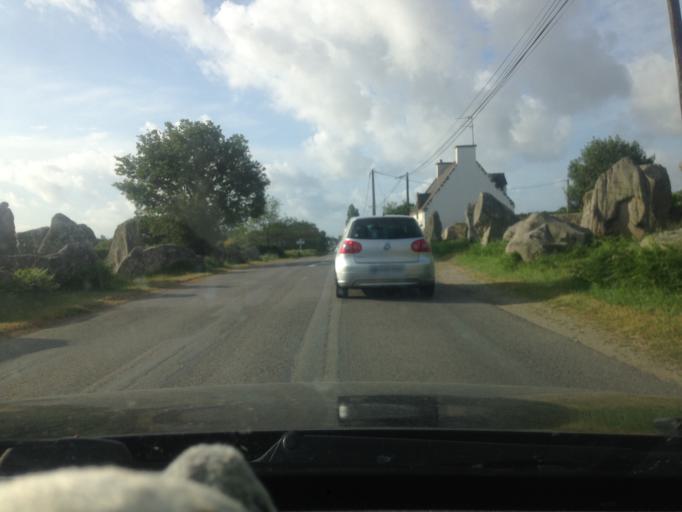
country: FR
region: Brittany
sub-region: Departement du Morbihan
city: Erdeven
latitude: 47.6348
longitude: -3.1493
